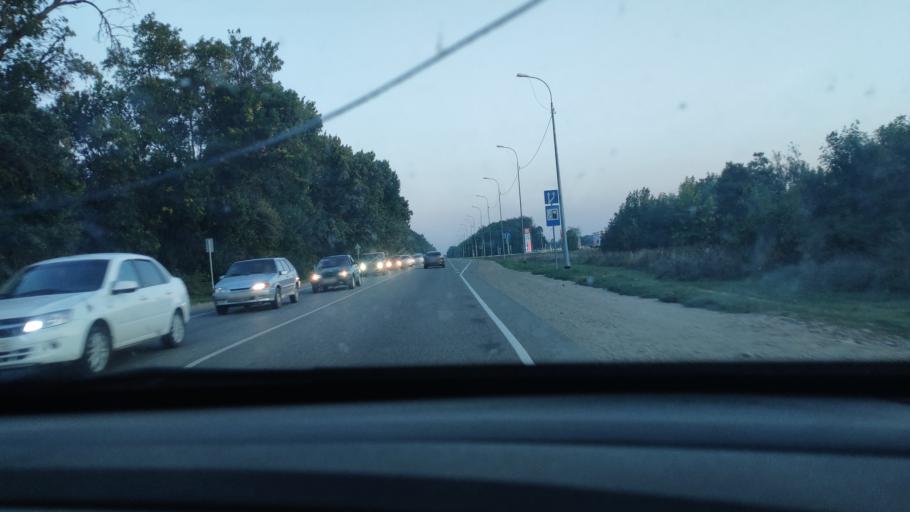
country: RU
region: Krasnodarskiy
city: Medvedovskaya
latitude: 45.4477
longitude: 38.9929
